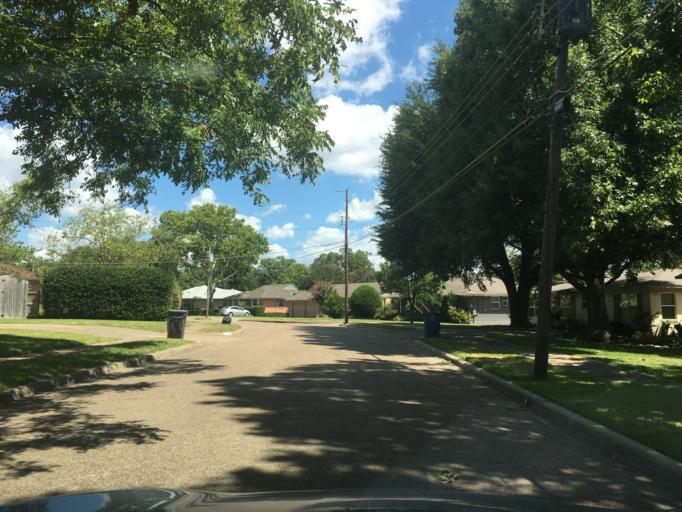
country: US
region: Texas
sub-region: Dallas County
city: Garland
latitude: 32.8695
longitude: -96.7016
